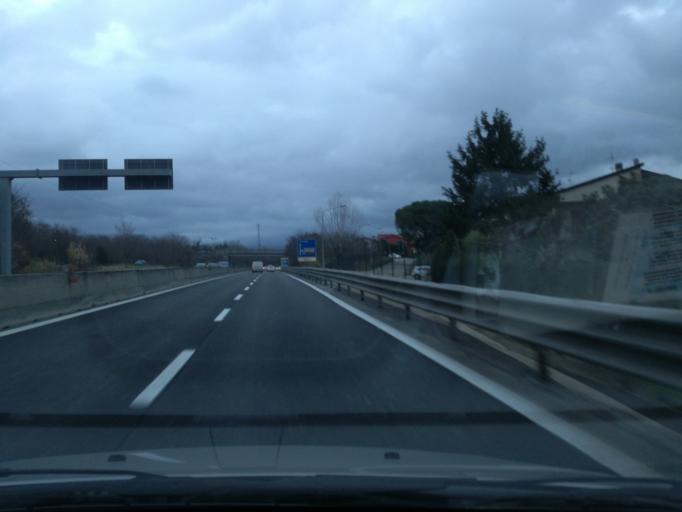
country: IT
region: Umbria
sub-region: Provincia di Perugia
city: Via Lippia
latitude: 43.0876
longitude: 12.4781
